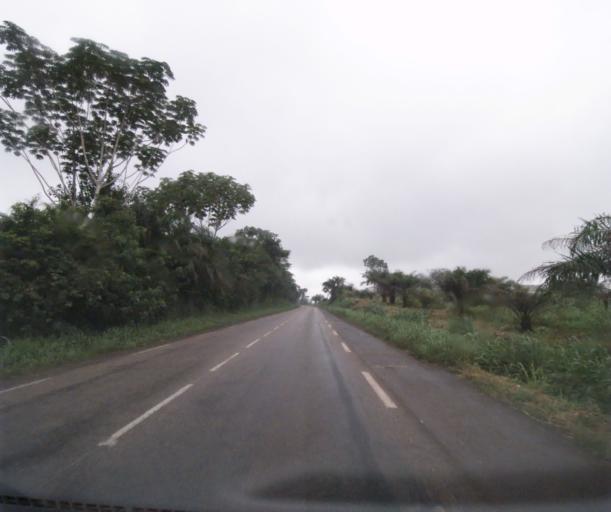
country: CM
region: Centre
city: Eseka
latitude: 3.8704
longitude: 10.6485
